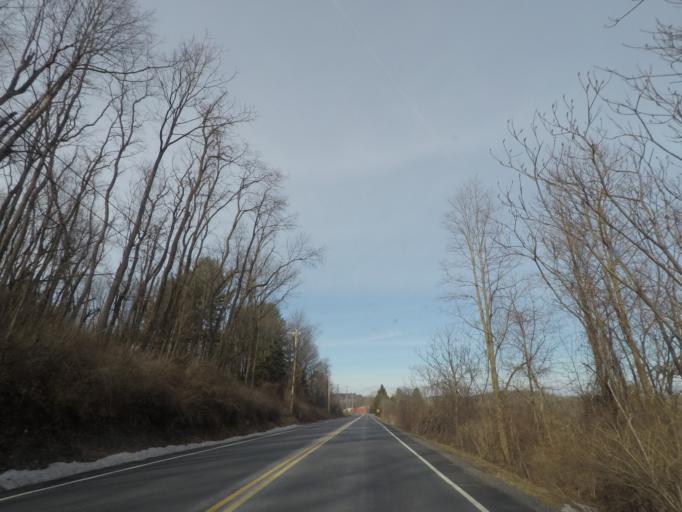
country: US
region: New York
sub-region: Columbia County
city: Valatie
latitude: 42.3876
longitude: -73.6433
